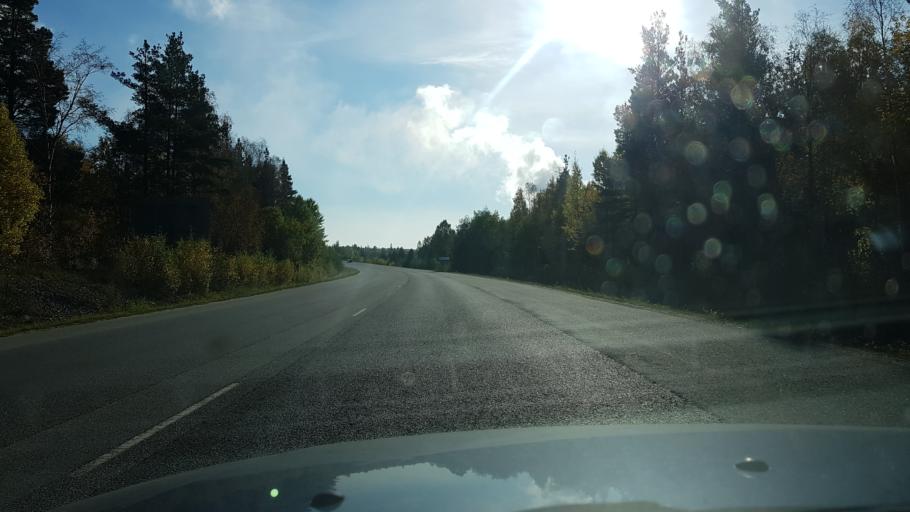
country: SE
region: Norrbotten
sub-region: Pitea Kommun
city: Pitea
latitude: 65.3282
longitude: 21.4288
